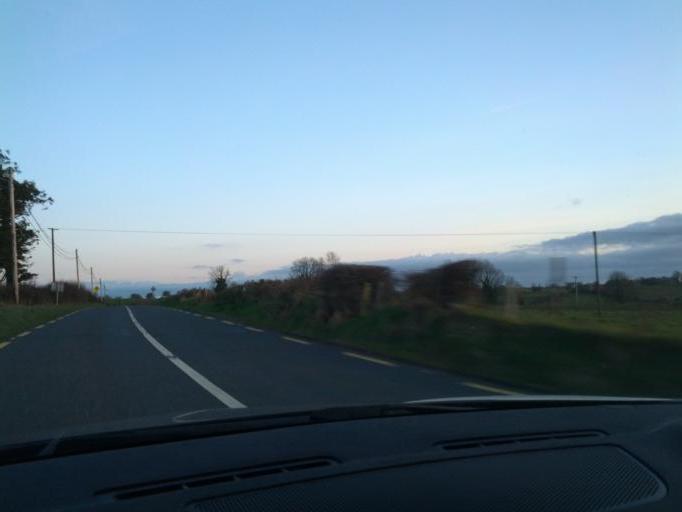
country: IE
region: Connaught
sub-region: Roscommon
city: Boyle
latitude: 53.9515
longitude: -8.2774
